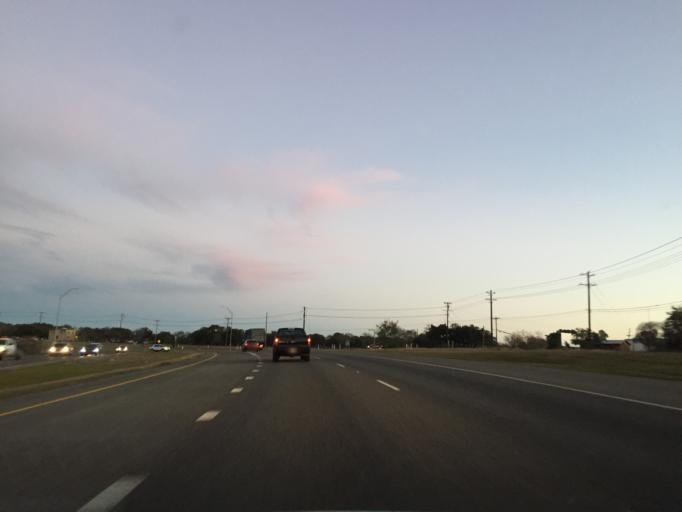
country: US
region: Texas
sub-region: Travis County
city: Jonestown
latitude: 30.5132
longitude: -97.8865
